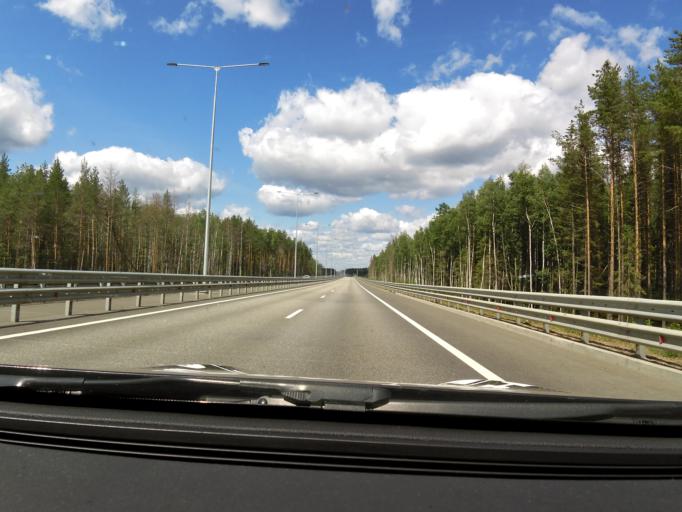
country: RU
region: Tverskaya
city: Krasnomayskiy
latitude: 57.4415
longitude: 34.4411
